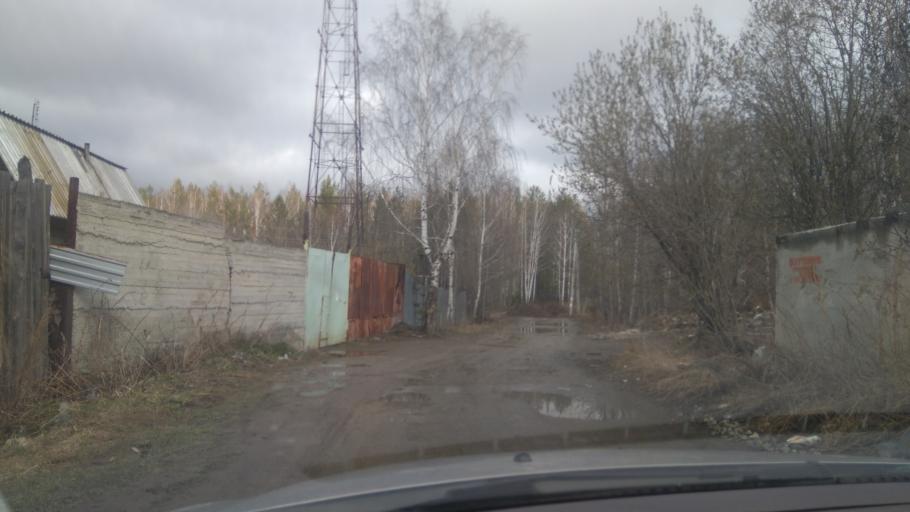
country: RU
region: Sverdlovsk
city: Verkhnyaya Pyshma
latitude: 56.9240
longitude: 60.5953
